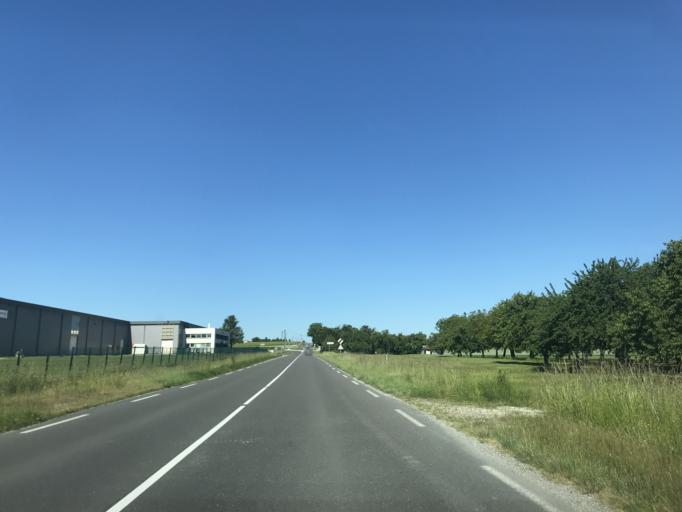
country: FR
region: Poitou-Charentes
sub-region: Departement de la Charente
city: Barbezieux-Saint-Hilaire
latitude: 45.4931
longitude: -0.2004
